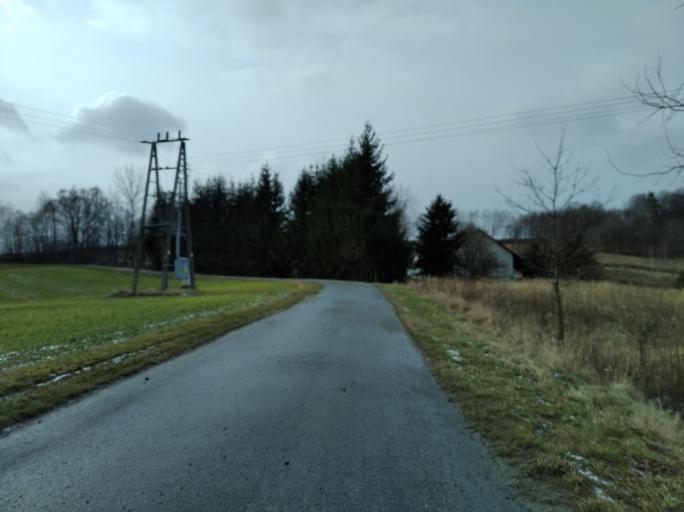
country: PL
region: Subcarpathian Voivodeship
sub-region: Powiat strzyzowski
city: Wysoka Strzyzowska
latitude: 49.8951
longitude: 21.7276
